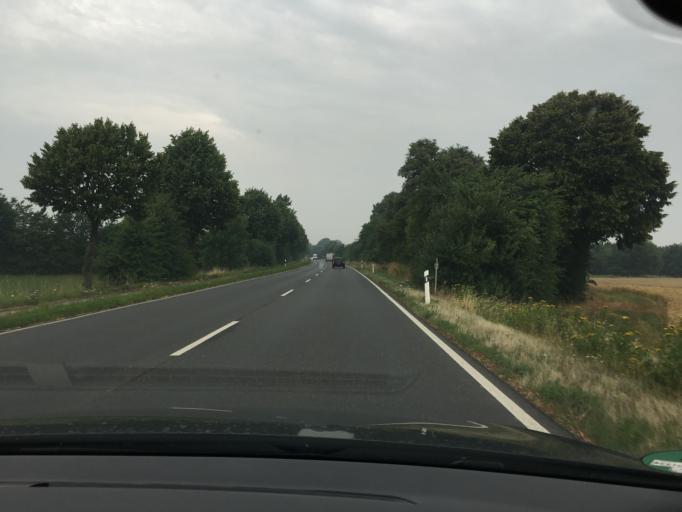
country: DE
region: North Rhine-Westphalia
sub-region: Regierungsbezirk Koln
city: Titz
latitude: 50.9466
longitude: 6.4212
